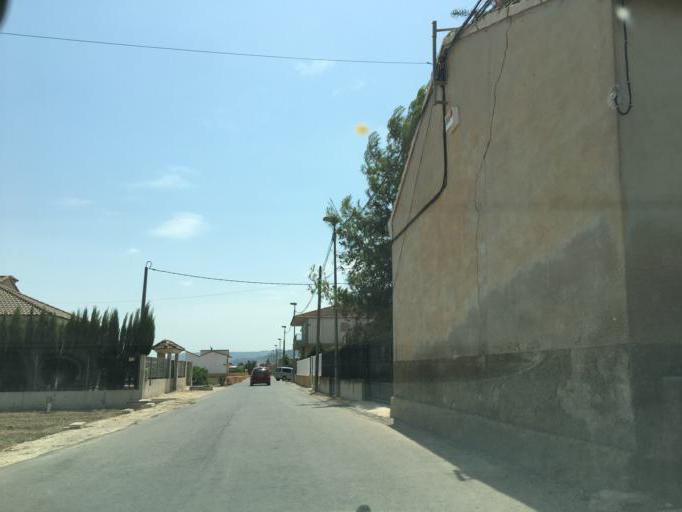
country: ES
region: Murcia
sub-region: Murcia
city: Santomera
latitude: 38.0330
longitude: -1.0524
